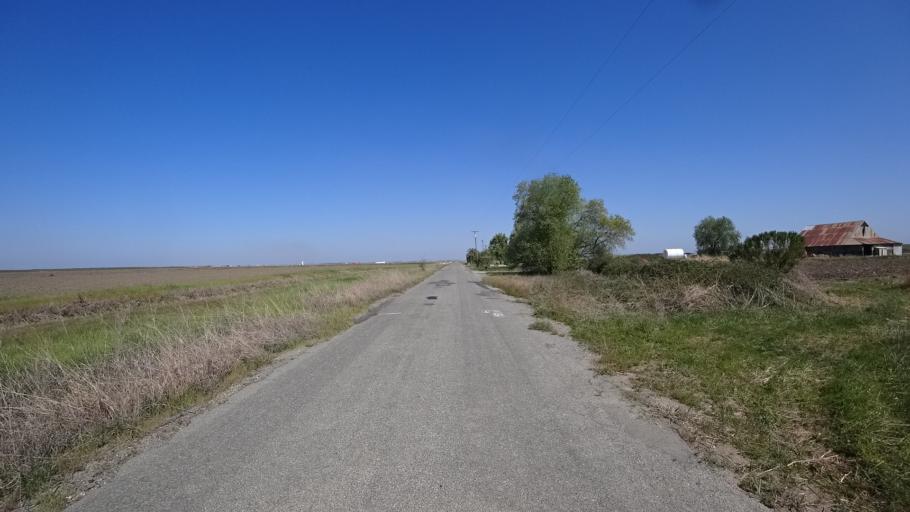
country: US
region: California
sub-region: Glenn County
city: Willows
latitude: 39.5107
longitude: -122.0373
